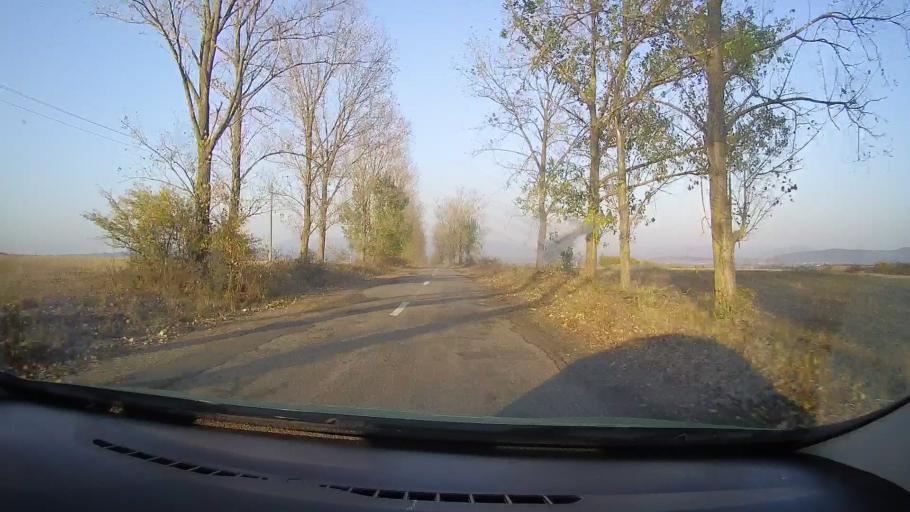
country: RO
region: Arad
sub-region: Comuna Barsa
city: Barsa
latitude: 46.3733
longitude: 22.0483
